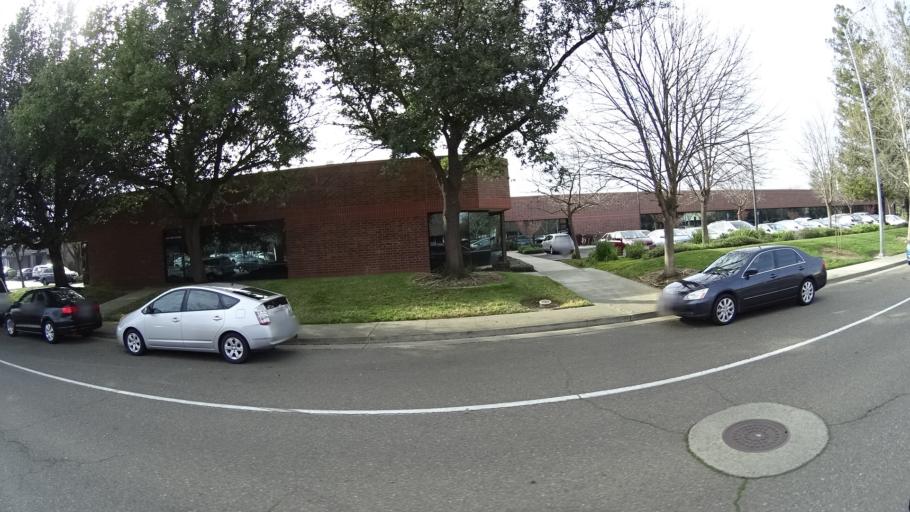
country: US
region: California
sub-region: Yolo County
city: Davis
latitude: 38.5434
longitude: -121.7275
